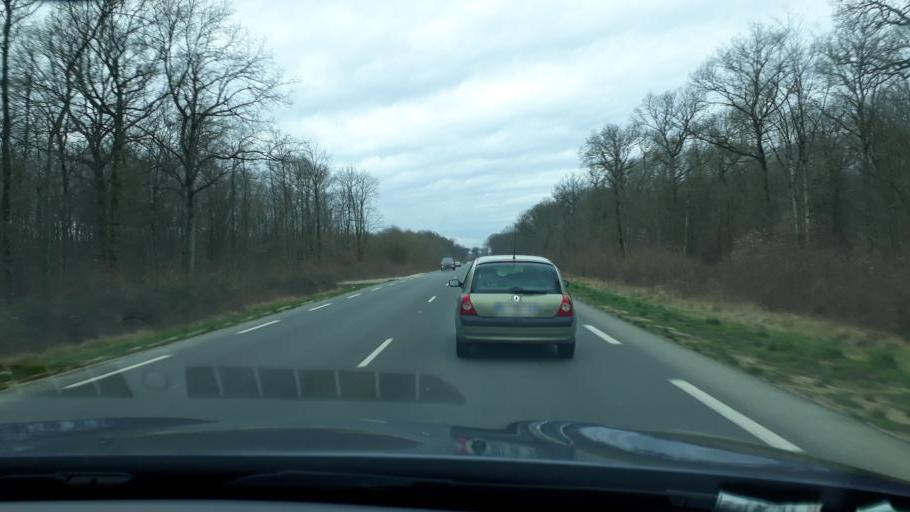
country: FR
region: Centre
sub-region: Departement du Loiret
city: Chanteau
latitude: 48.0044
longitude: 1.9505
